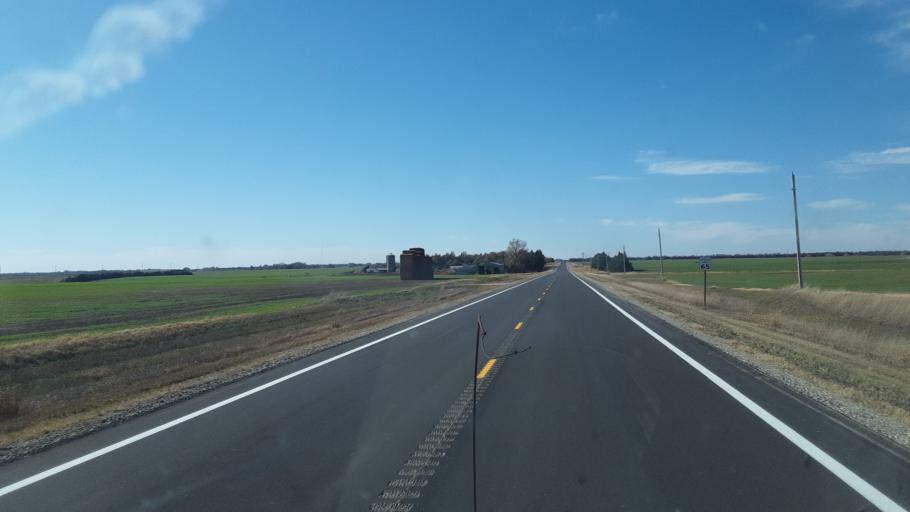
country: US
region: Kansas
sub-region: Rice County
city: Lyons
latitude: 38.3766
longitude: -98.0925
